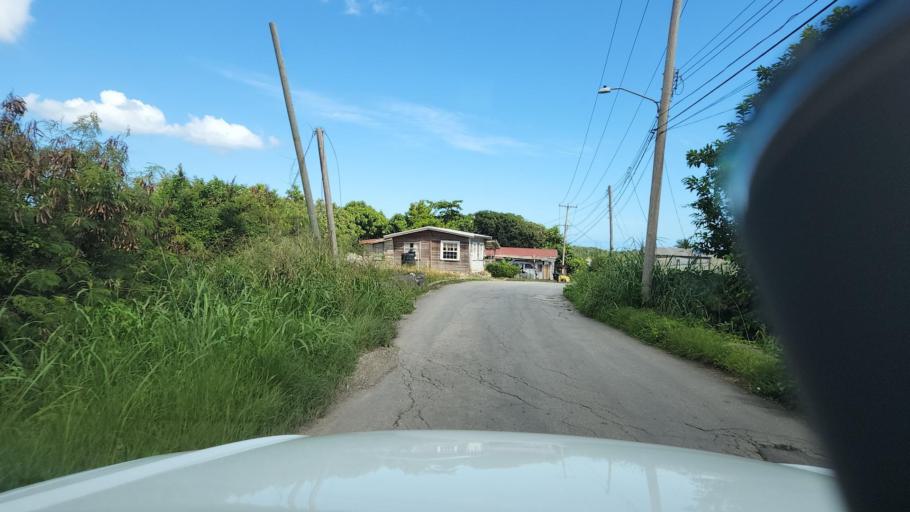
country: BB
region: Saint Thomas
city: Welchman Hall
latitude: 13.2071
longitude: -59.5572
